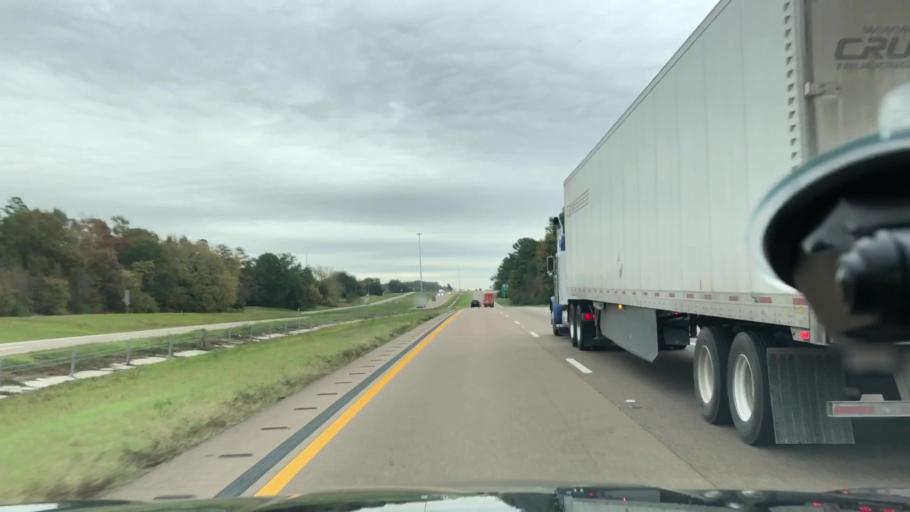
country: US
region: Texas
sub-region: Titus County
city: Mount Pleasant
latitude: 33.1663
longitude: -95.0107
